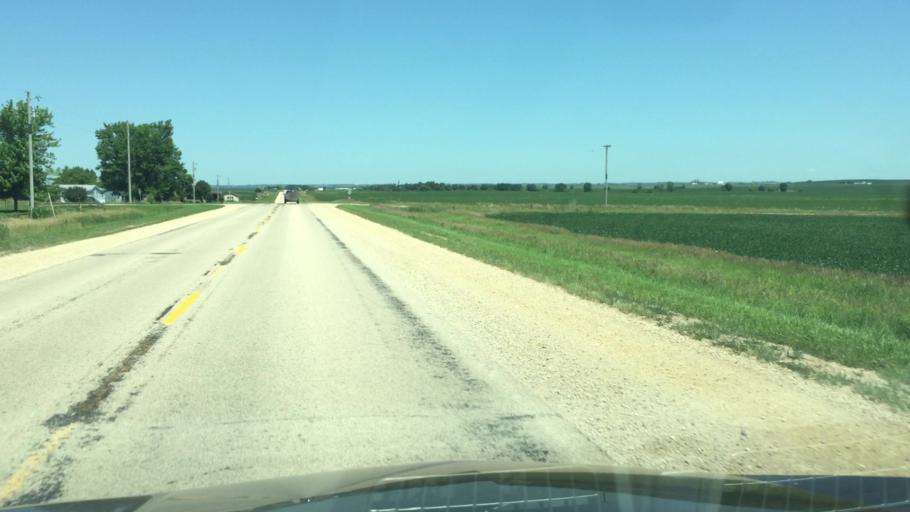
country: US
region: Iowa
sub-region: Cedar County
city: Mechanicsville
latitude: 41.9312
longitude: -91.1518
